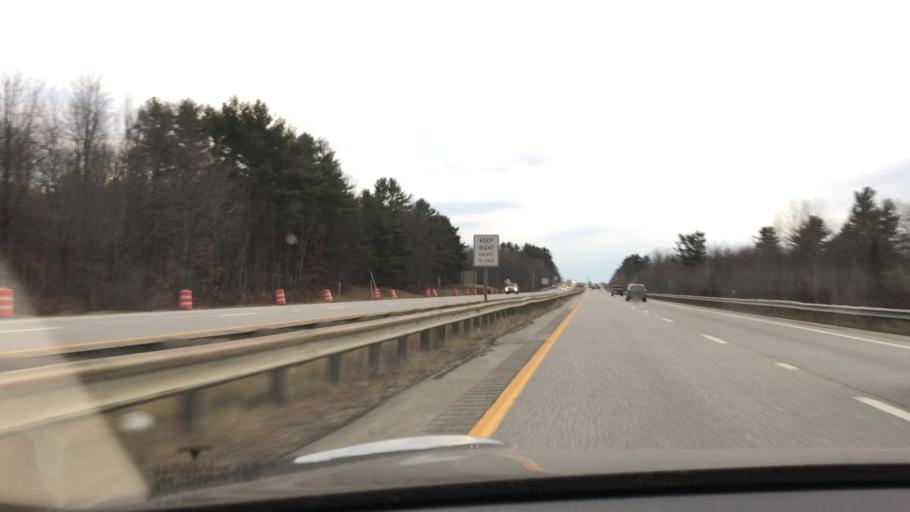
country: US
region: Maine
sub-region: Kennebec County
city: Hallowell
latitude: 44.2937
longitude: -69.8073
